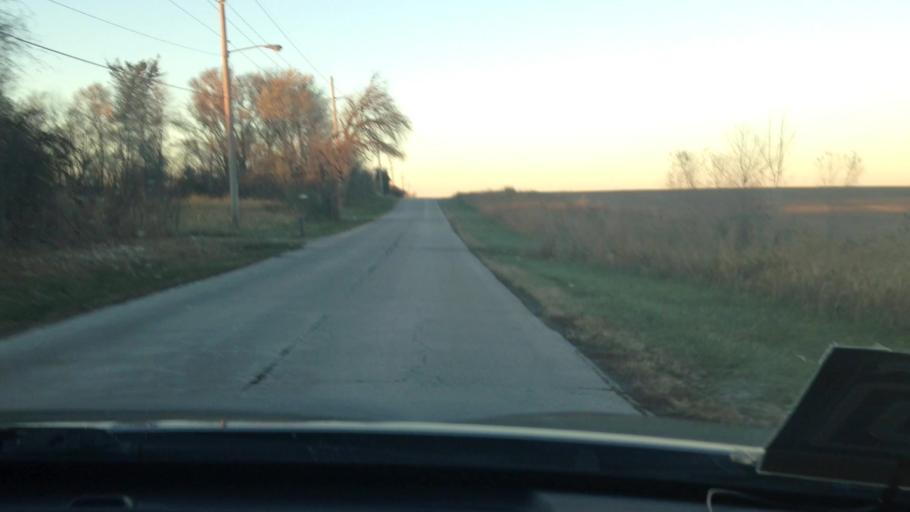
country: US
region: Kansas
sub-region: Wyandotte County
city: Bonner Springs
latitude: 39.1181
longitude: -94.8537
